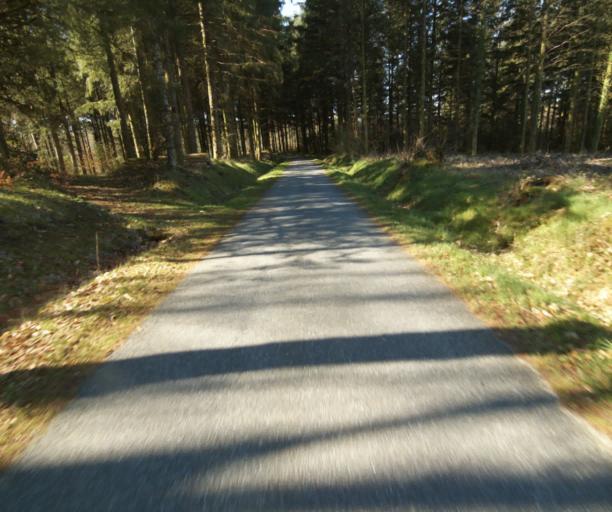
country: FR
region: Limousin
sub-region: Departement de la Correze
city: Correze
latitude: 45.2916
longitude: 1.9189
